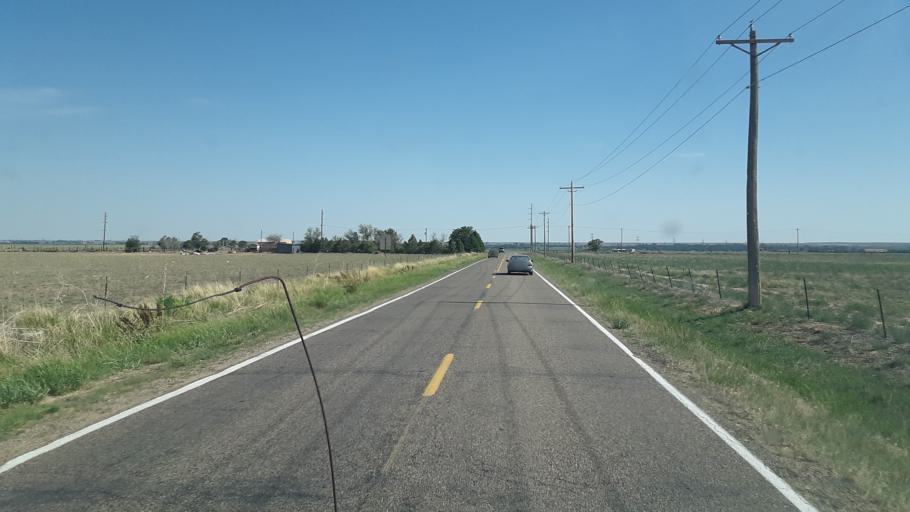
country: US
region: Colorado
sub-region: Crowley County
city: Ordway
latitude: 38.1444
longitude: -103.8568
